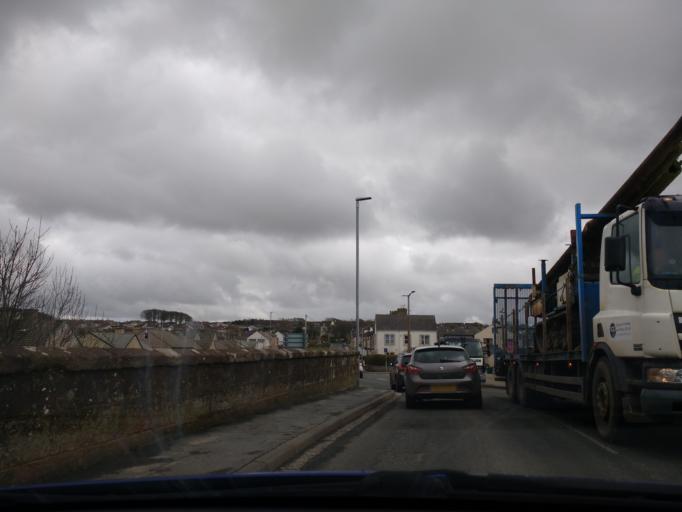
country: GB
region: England
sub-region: Cumbria
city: Maryport
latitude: 54.7129
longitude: -3.4898
